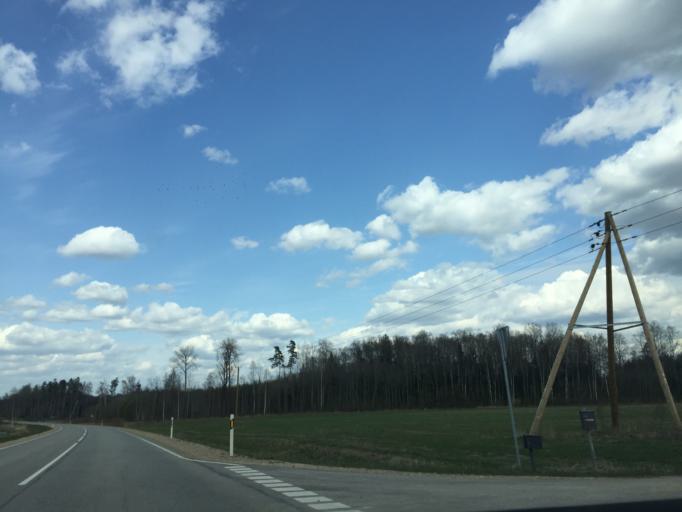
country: LV
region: Skriveri
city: Skriveri
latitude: 56.7575
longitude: 25.1707
